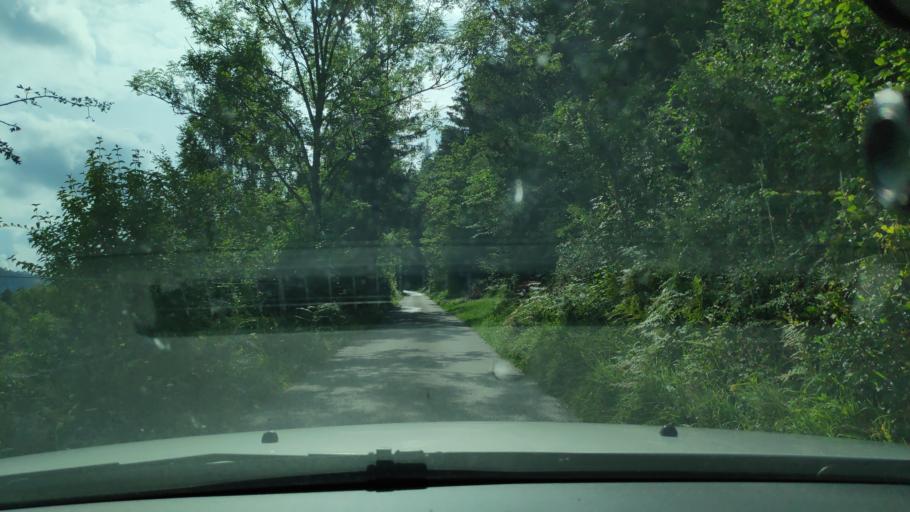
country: AT
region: Lower Austria
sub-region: Politischer Bezirk Wiener Neustadt
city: Miesenbach
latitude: 47.8332
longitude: 15.9752
